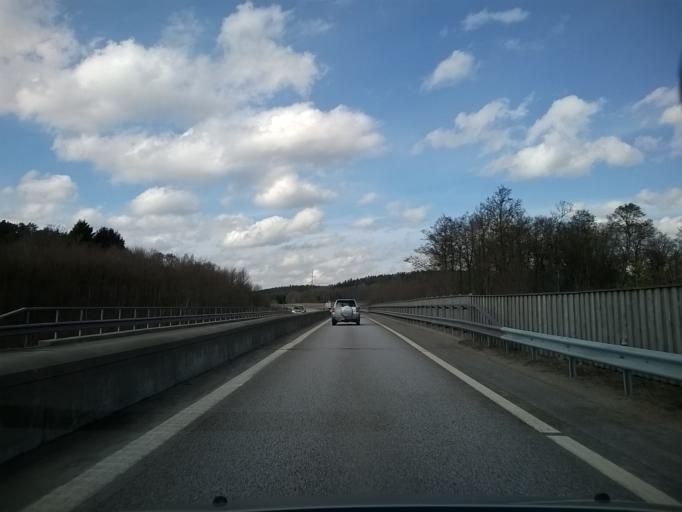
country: SE
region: Vaestra Goetaland
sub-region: Orust
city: Henan
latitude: 58.3484
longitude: 11.7482
